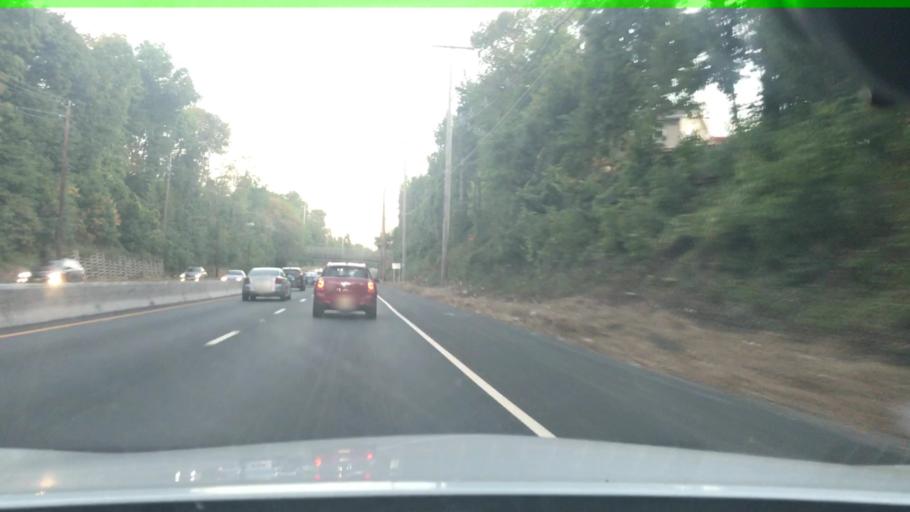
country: US
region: New Jersey
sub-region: Passaic County
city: Hawthorne
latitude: 40.9654
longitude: -74.1509
